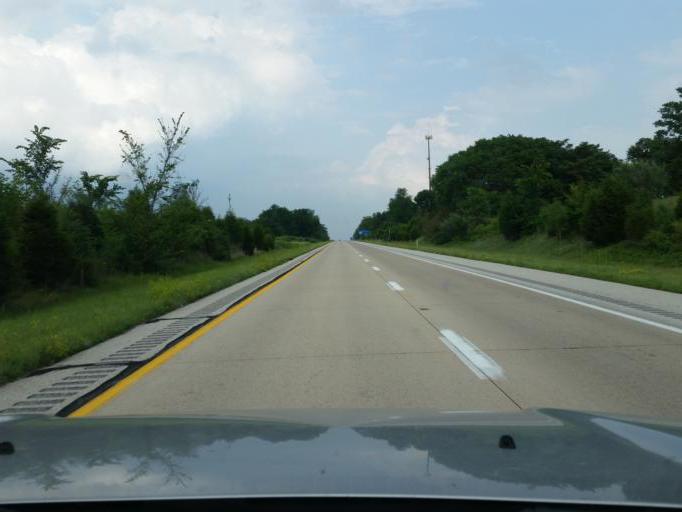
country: US
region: Pennsylvania
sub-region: Adams County
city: Gettysburg
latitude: 39.7652
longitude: -77.2579
